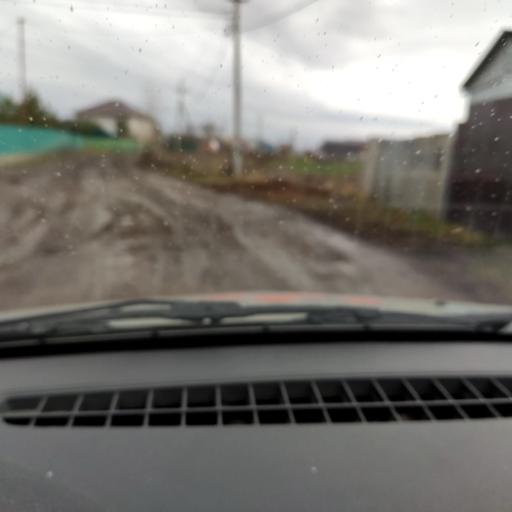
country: RU
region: Bashkortostan
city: Mikhaylovka
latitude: 54.8386
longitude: 55.9458
